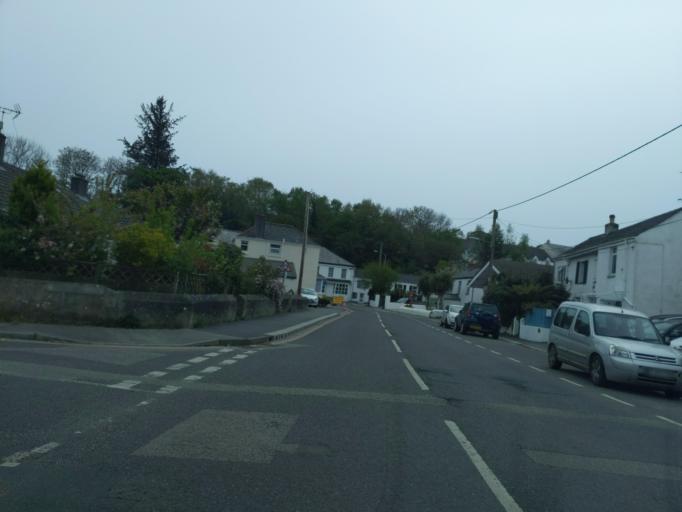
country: GB
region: England
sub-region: Cornwall
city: Par
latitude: 50.3514
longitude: -4.7108
